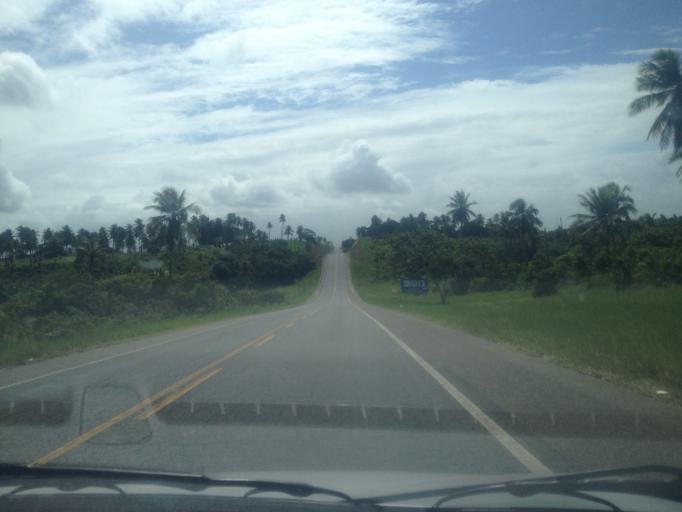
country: BR
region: Bahia
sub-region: Conde
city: Conde
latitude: -11.8371
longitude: -37.6353
